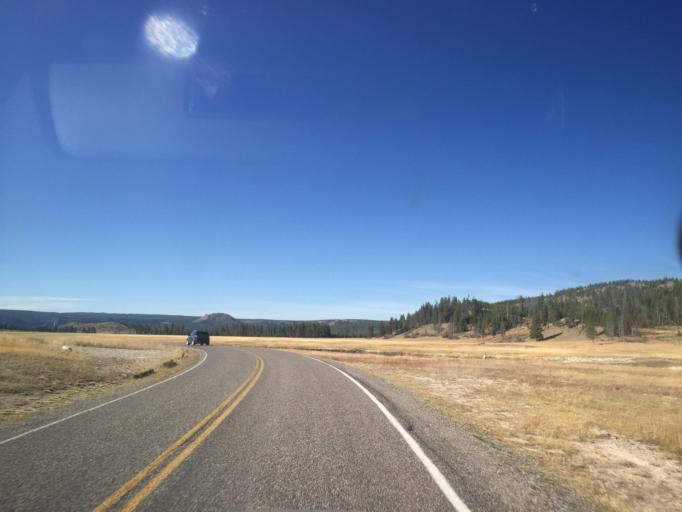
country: US
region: Montana
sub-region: Gallatin County
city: West Yellowstone
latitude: 44.5768
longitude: -110.8312
